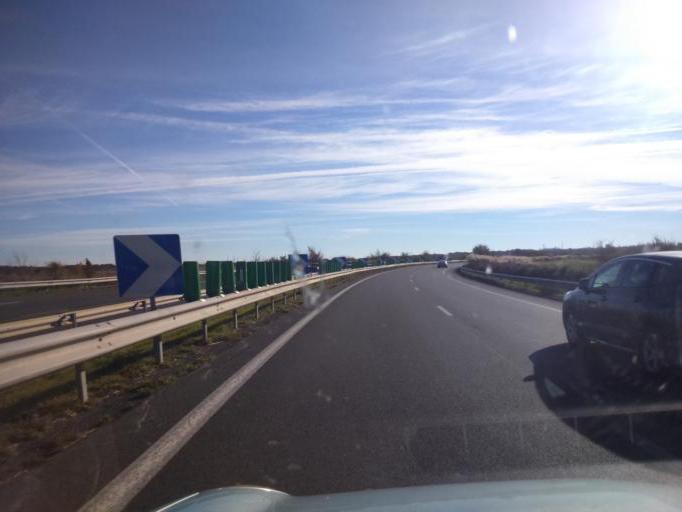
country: FR
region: Poitou-Charentes
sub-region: Departement de la Charente-Maritime
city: Saint-Laurent-de-la-Pree
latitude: 45.9801
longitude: -1.0002
